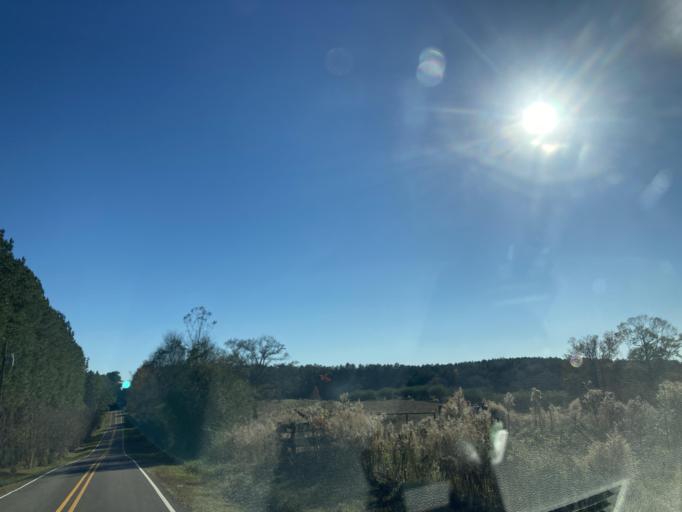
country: US
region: Mississippi
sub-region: Lamar County
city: Sumrall
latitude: 31.3649
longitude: -89.5694
